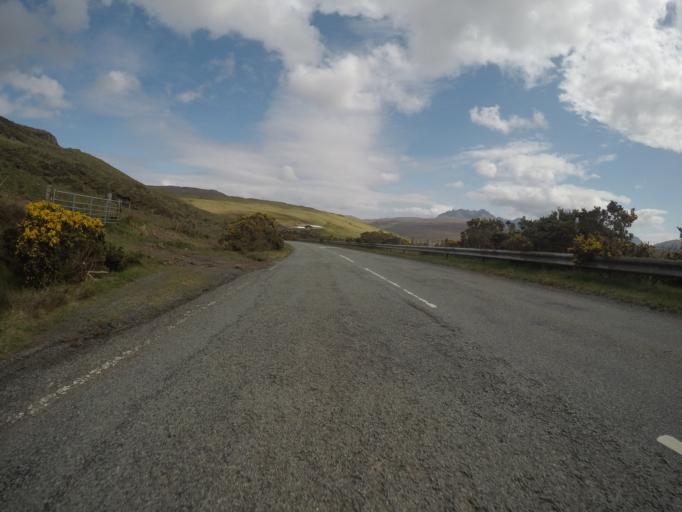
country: GB
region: Scotland
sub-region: Highland
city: Isle of Skye
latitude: 57.3045
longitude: -6.3056
